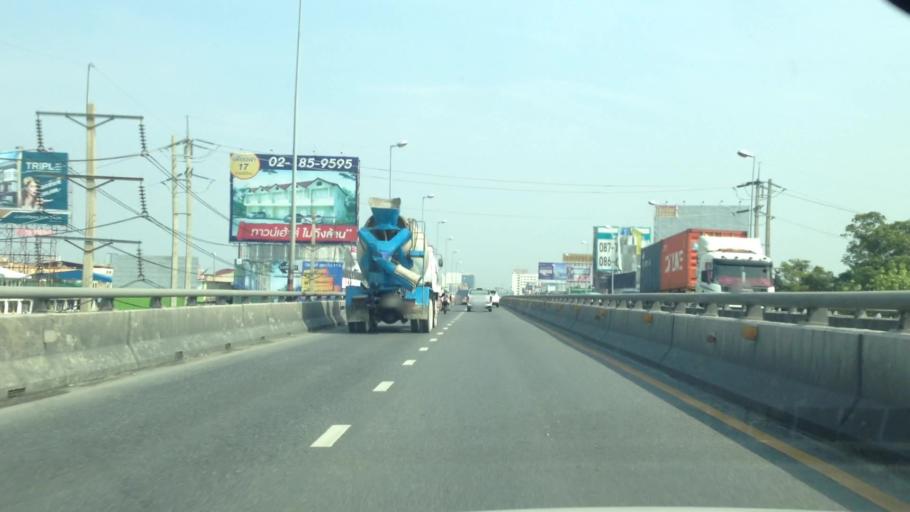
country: TH
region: Bangkok
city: Bang Na
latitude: 13.6287
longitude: 100.6274
